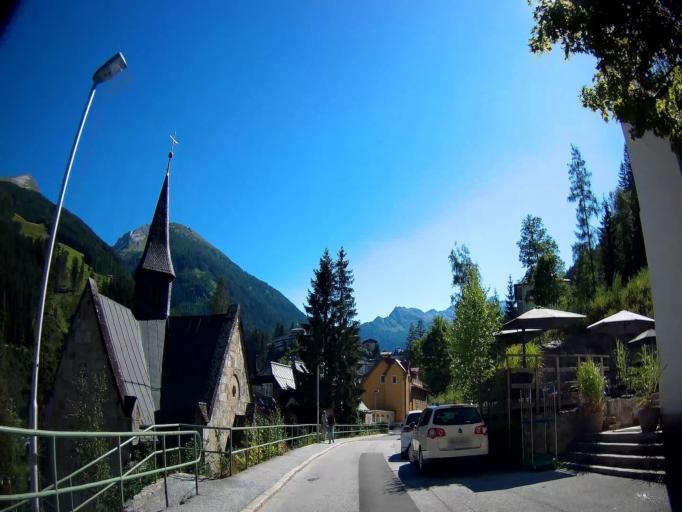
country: AT
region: Salzburg
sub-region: Politischer Bezirk Sankt Johann im Pongau
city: Bad Gastein
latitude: 47.1168
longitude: 13.1344
